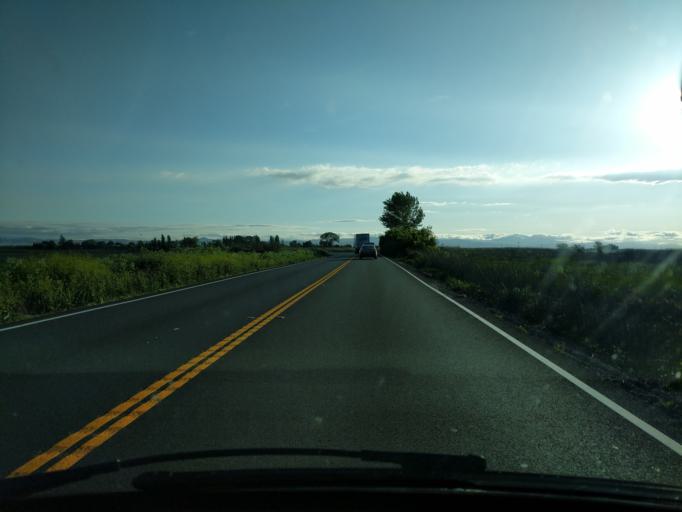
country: US
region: California
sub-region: Contra Costa County
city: Discovery Bay
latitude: 37.8970
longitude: -121.4799
